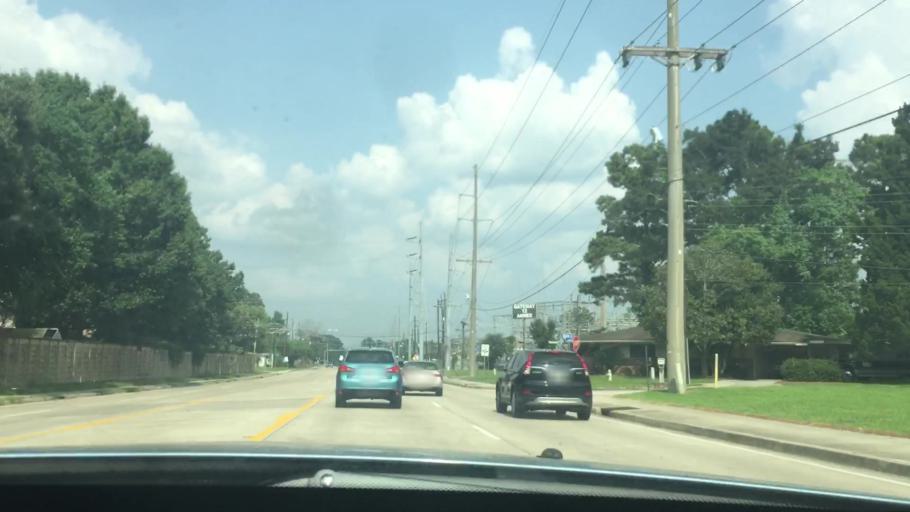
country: US
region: Louisiana
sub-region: East Baton Rouge Parish
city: Westminster
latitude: 30.4351
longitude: -91.0639
